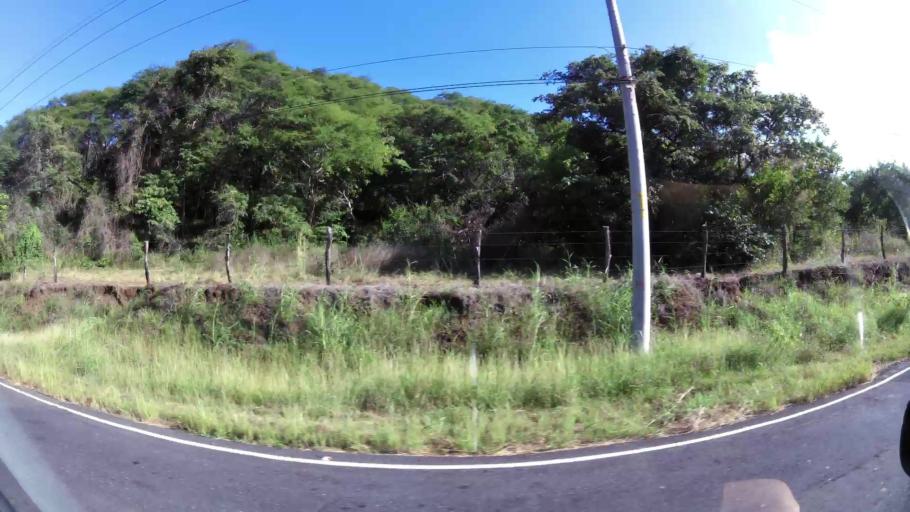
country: CR
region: Guanacaste
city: Sardinal
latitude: 10.5738
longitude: -85.6305
